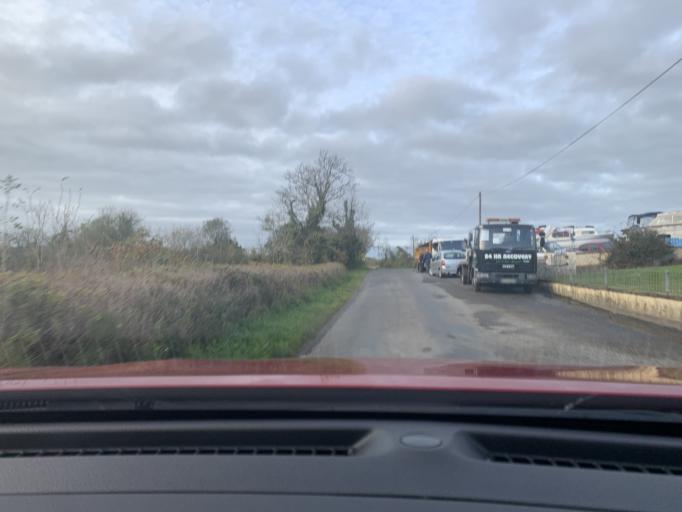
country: IE
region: Connaught
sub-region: Roscommon
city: Ballaghaderreen
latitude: 53.9992
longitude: -8.6068
